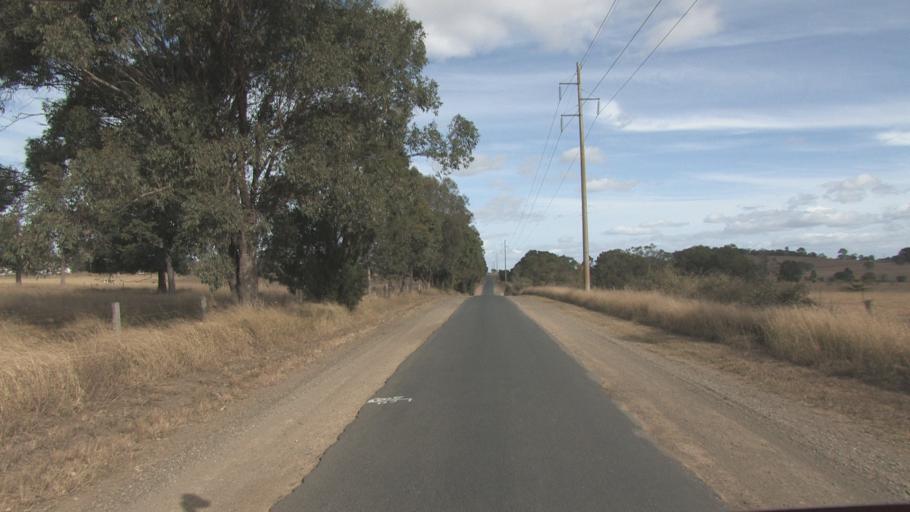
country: AU
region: Queensland
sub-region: Logan
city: Cedar Vale
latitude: -27.9164
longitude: 153.0135
